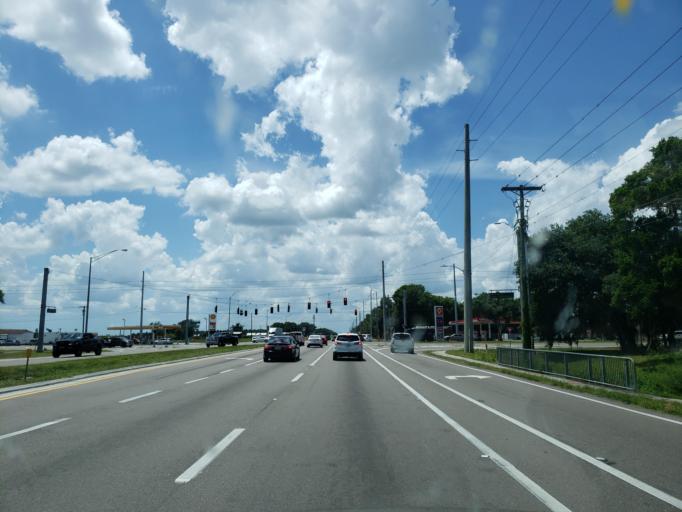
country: US
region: Florida
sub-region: Hillsborough County
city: Plant City
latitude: 27.9378
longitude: -82.1201
